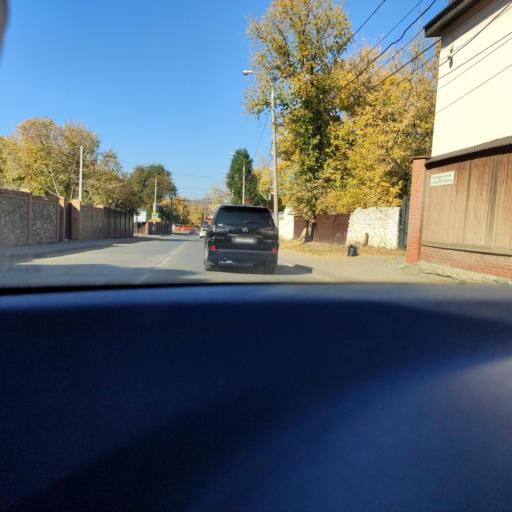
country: RU
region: Samara
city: Samara
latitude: 53.2737
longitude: 50.1916
